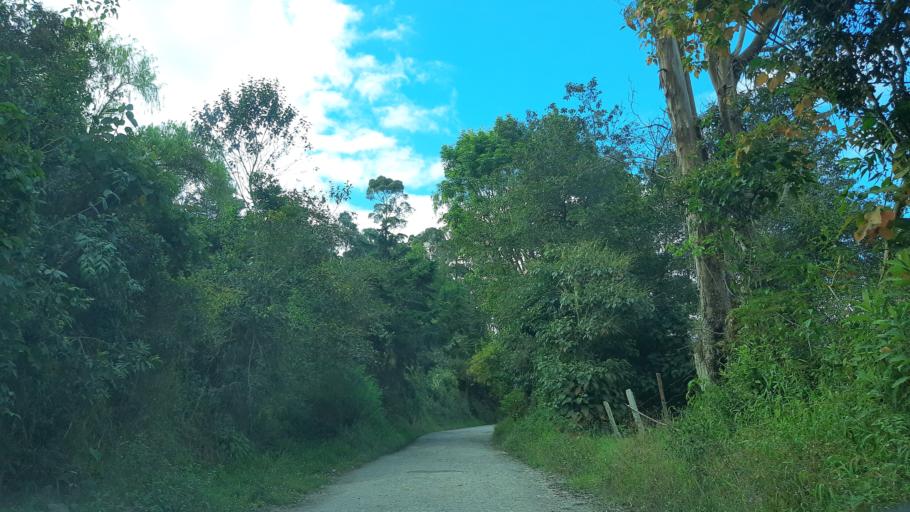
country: CO
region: Cundinamarca
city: Tenza
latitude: 5.0437
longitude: -73.4245
